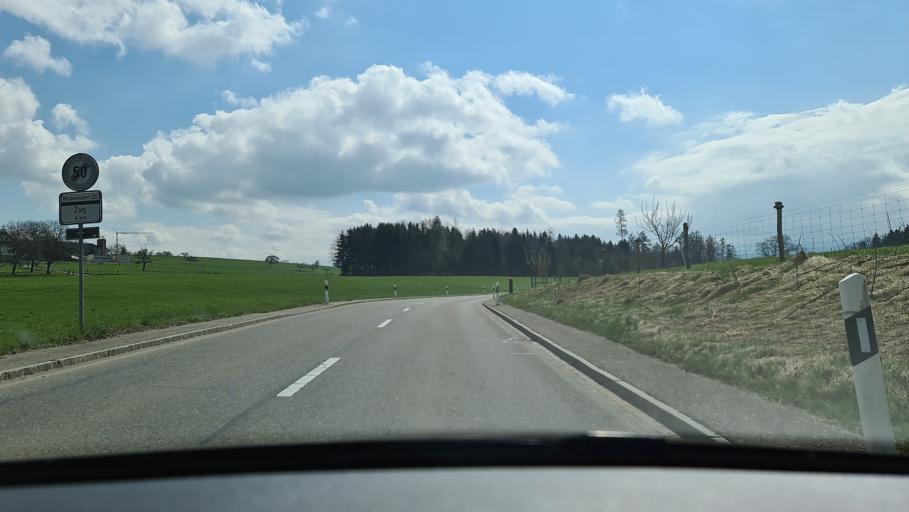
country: CH
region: Zug
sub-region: Zug
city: Steinhausen
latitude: 47.2212
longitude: 8.5006
